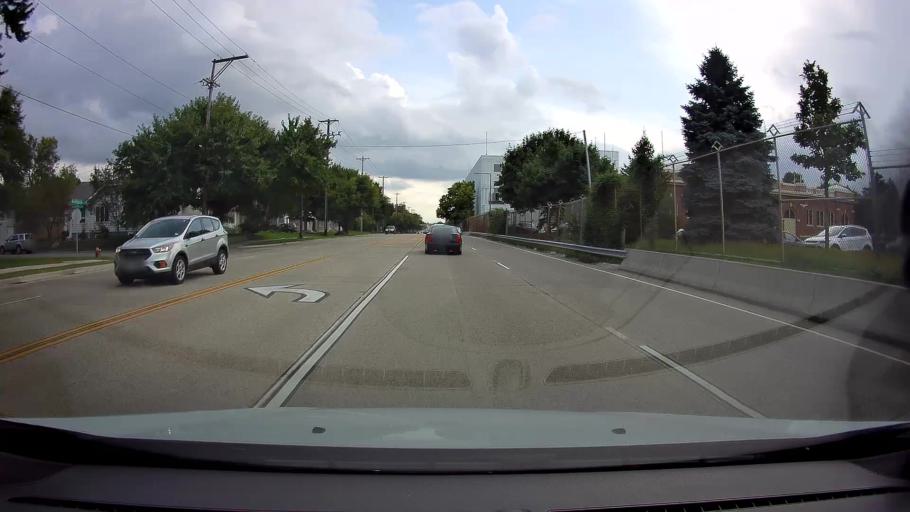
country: US
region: Minnesota
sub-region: Ramsey County
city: Falcon Heights
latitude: 44.9849
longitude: -93.1670
